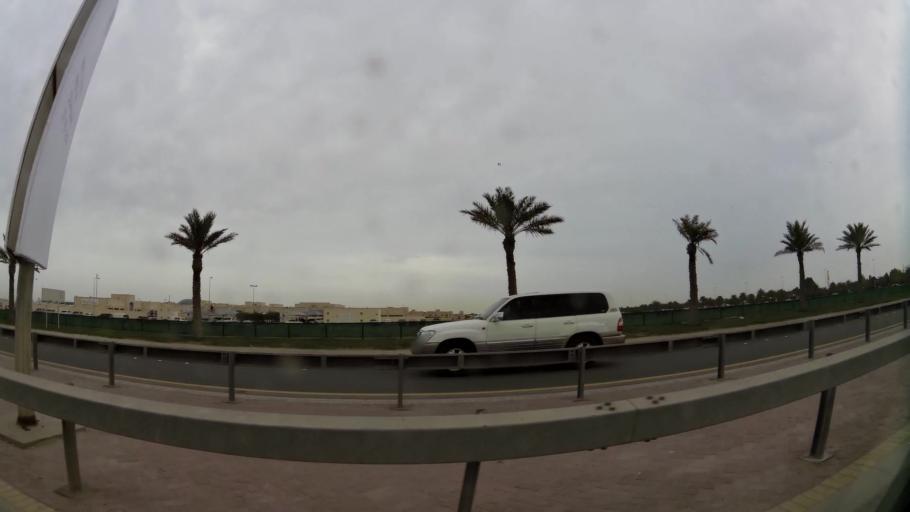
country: BH
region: Northern
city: Ar Rifa'
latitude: 26.0987
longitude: 50.5444
